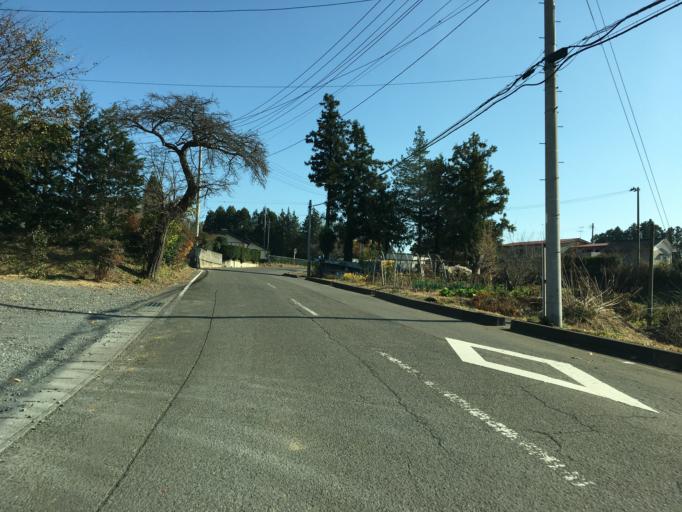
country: JP
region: Fukushima
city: Nihommatsu
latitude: 37.5778
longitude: 140.3964
